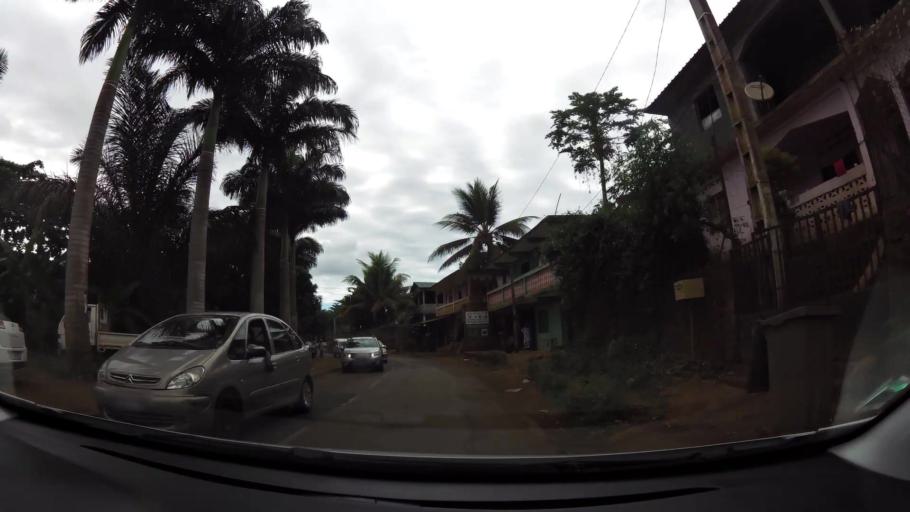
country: YT
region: Chiconi
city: Chiconi
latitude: -12.8331
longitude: 45.1150
